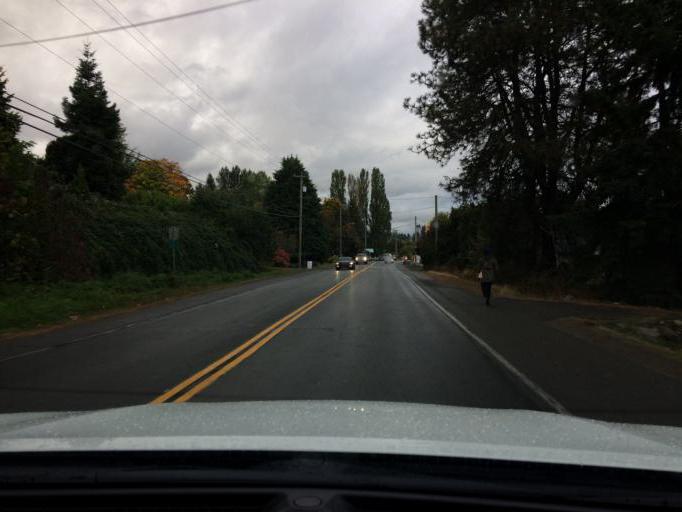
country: CA
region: British Columbia
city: Courtenay
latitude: 49.6426
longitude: -124.9344
